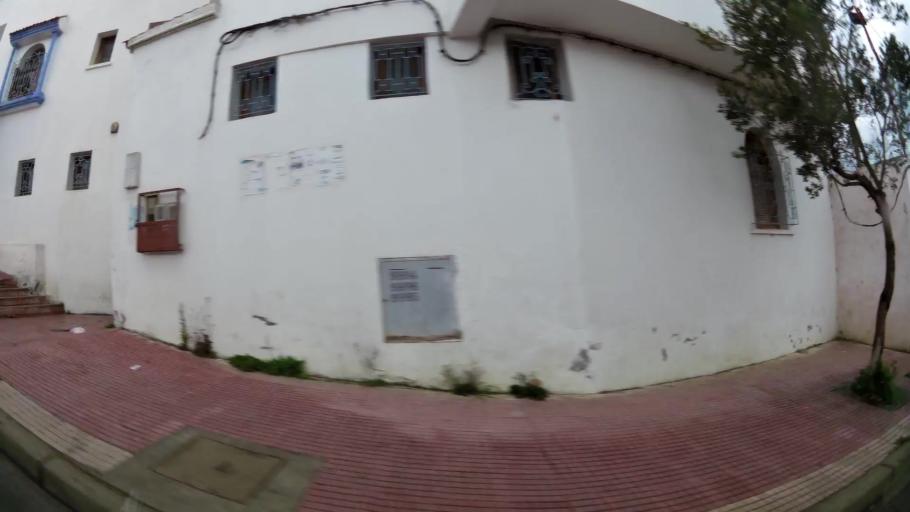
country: MA
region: Tanger-Tetouan
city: Chefchaouene
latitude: 35.1701
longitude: -5.2729
